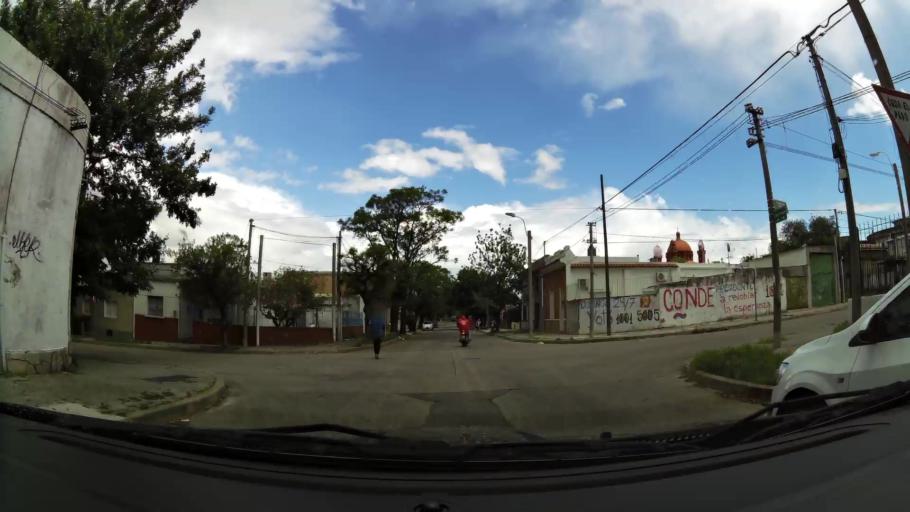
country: UY
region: Montevideo
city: Montevideo
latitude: -34.8552
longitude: -56.1678
